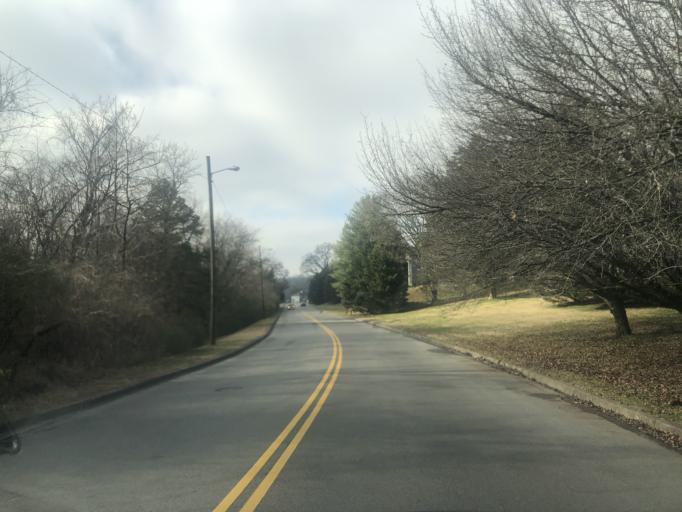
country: US
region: Tennessee
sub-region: Rutherford County
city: La Vergne
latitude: 36.0762
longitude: -86.6440
